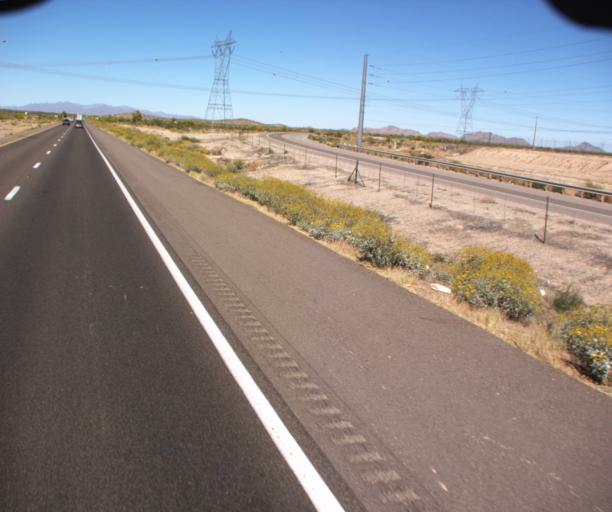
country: US
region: Arizona
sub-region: Maricopa County
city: Buckeye
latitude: 33.2262
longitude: -112.6425
